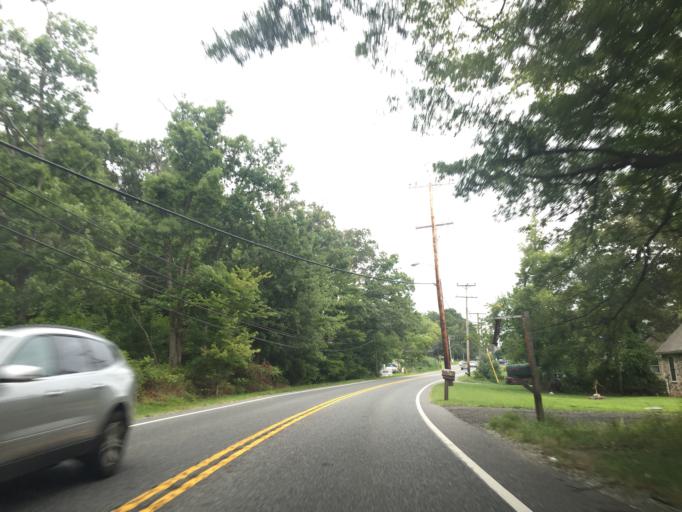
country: US
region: Maryland
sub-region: Harford County
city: Joppatowne
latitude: 39.4287
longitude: -76.3721
